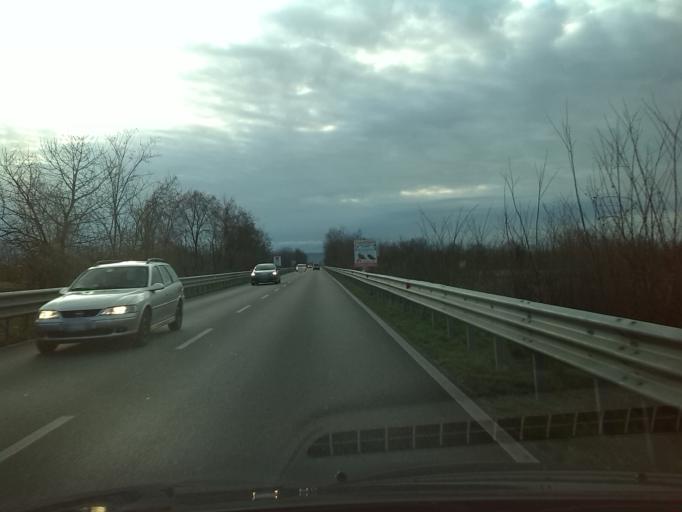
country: IT
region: Friuli Venezia Giulia
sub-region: Provincia di Udine
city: San Giovanni al Natisone
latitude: 45.9561
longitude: 13.4274
